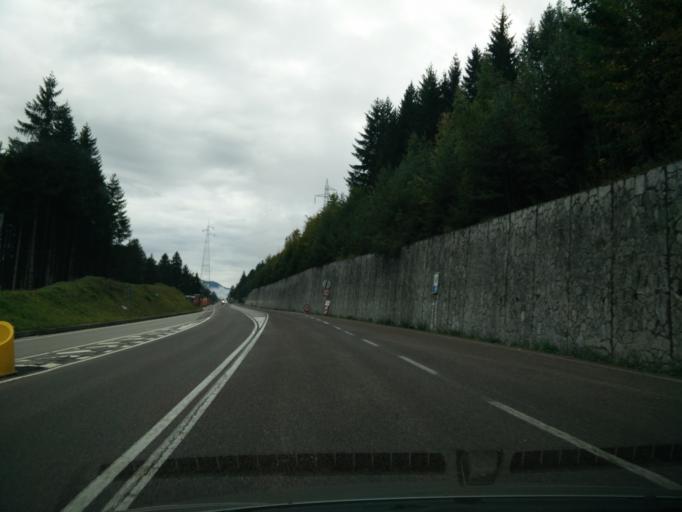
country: IT
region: Veneto
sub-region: Provincia di Belluno
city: Perarolo di Cadore
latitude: 46.3954
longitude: 12.3704
